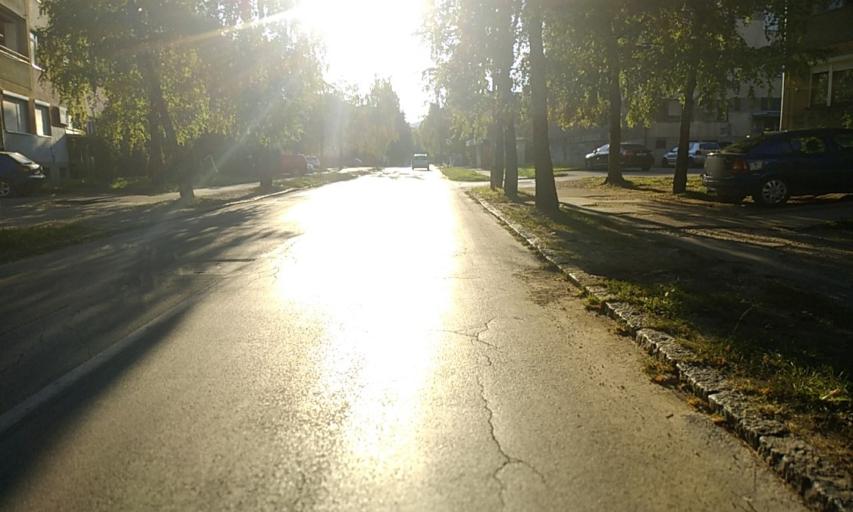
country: BA
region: Republika Srpska
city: Mejdan - Obilicevo
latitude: 44.7644
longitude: 17.1940
